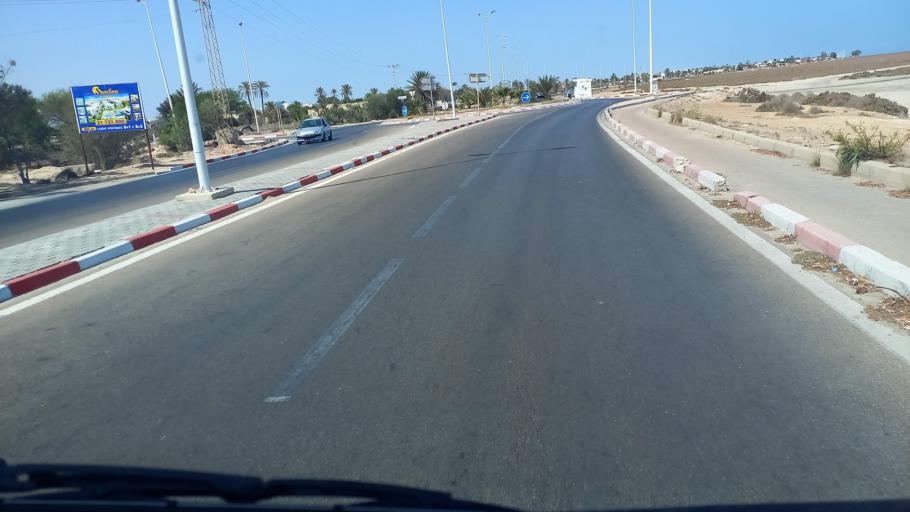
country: TN
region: Madanin
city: Midoun
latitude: 33.8689
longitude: 10.9462
